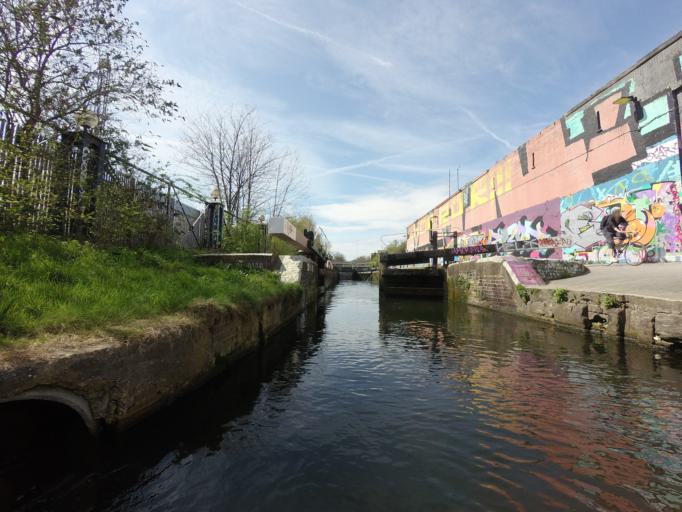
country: GB
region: England
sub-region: Greater London
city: Hackney
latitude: 51.5406
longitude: -0.0242
